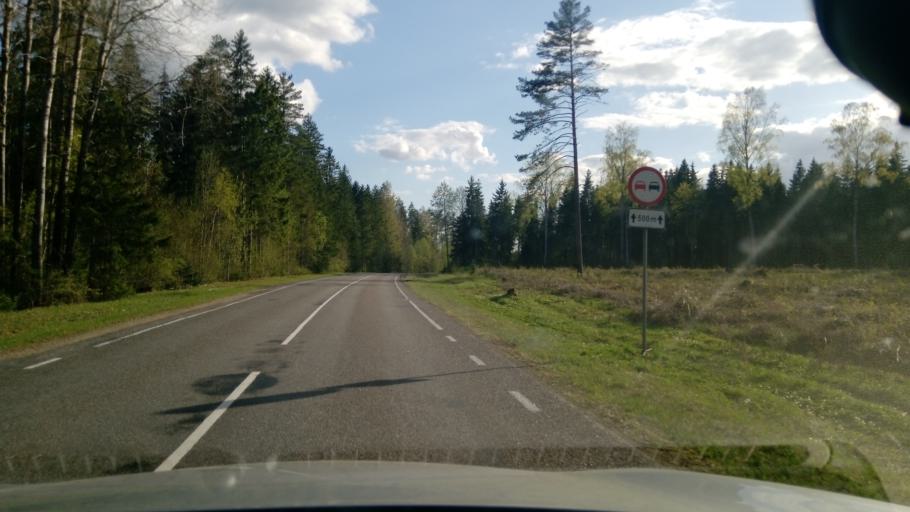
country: EE
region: Jaervamaa
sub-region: Jaerva-Jaani vald
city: Jarva-Jaani
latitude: 59.0545
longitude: 25.9182
